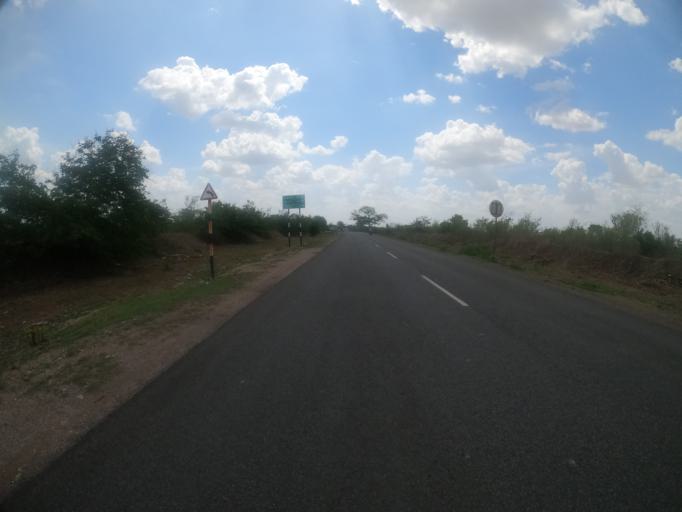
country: IN
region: Telangana
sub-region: Rangareddi
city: Sriramnagar
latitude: 17.3120
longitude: 78.1746
